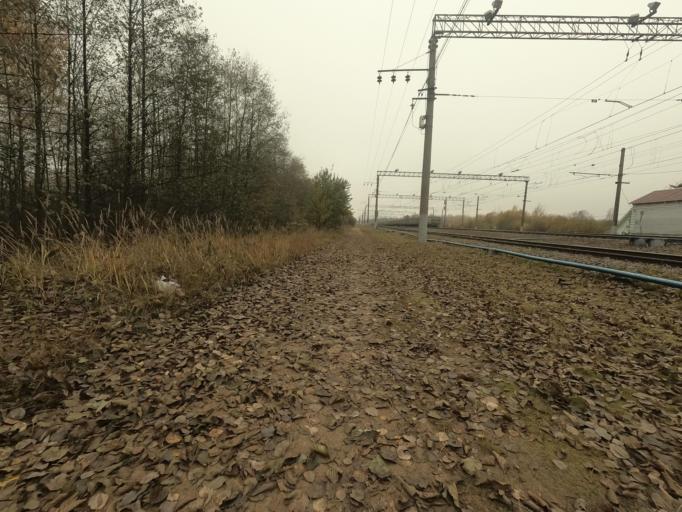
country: RU
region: Leningrad
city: Pavlovo
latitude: 59.7663
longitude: 30.9569
